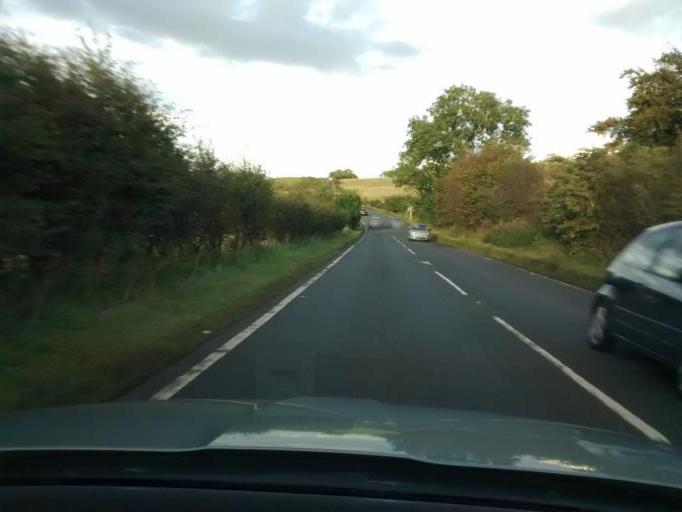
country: GB
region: Scotland
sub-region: Renfrewshire
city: Howwood
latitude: 55.8021
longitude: -4.5876
